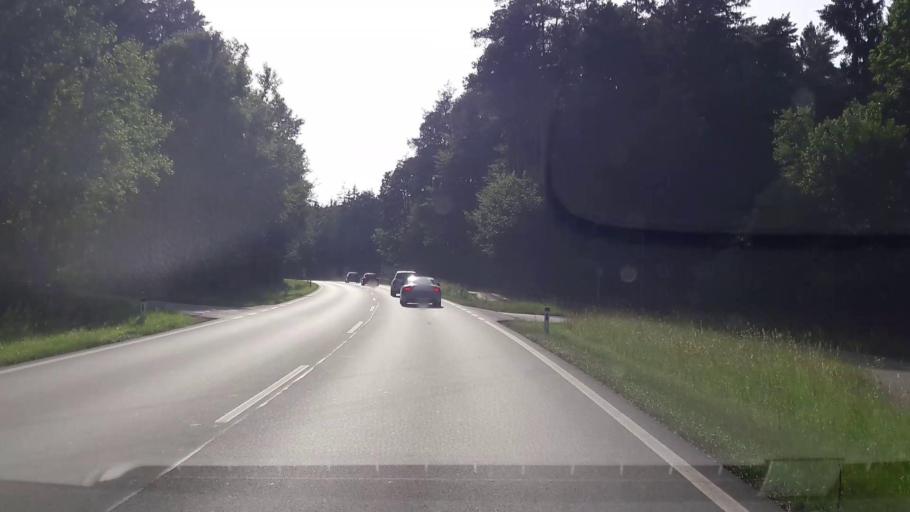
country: AT
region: Burgenland
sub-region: Politischer Bezirk Oberwart
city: Kemeten
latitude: 47.2824
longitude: 16.1406
